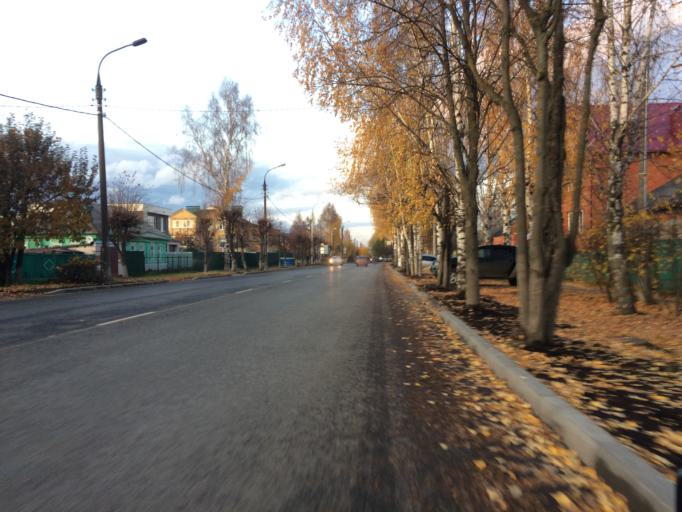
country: RU
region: Mariy-El
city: Yoshkar-Ola
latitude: 56.6514
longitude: 47.8958
